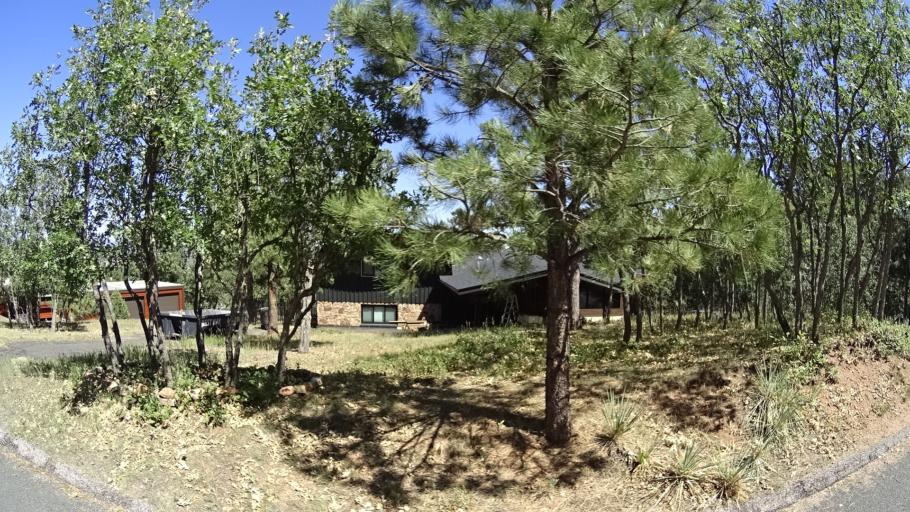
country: US
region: Colorado
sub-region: El Paso County
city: Colorado Springs
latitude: 38.7825
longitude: -104.8555
